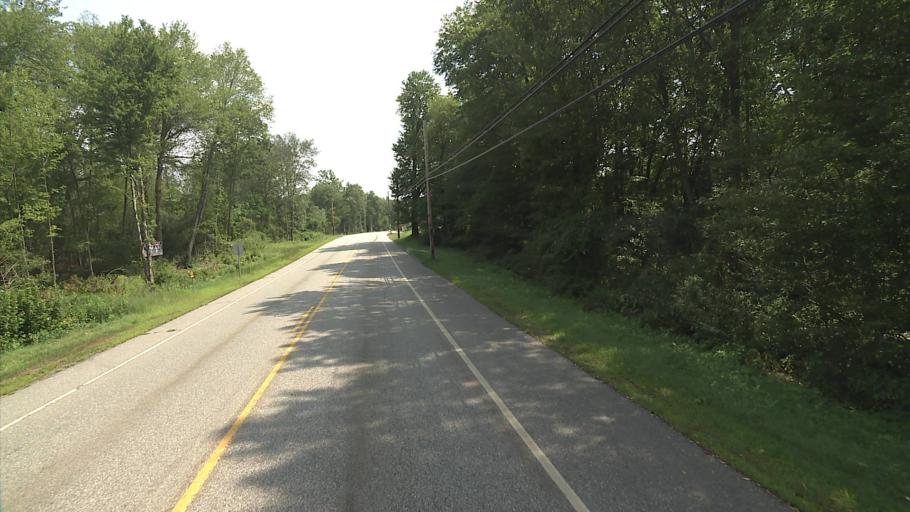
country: US
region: Connecticut
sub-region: New London County
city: Montville Center
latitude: 41.5063
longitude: -72.1386
